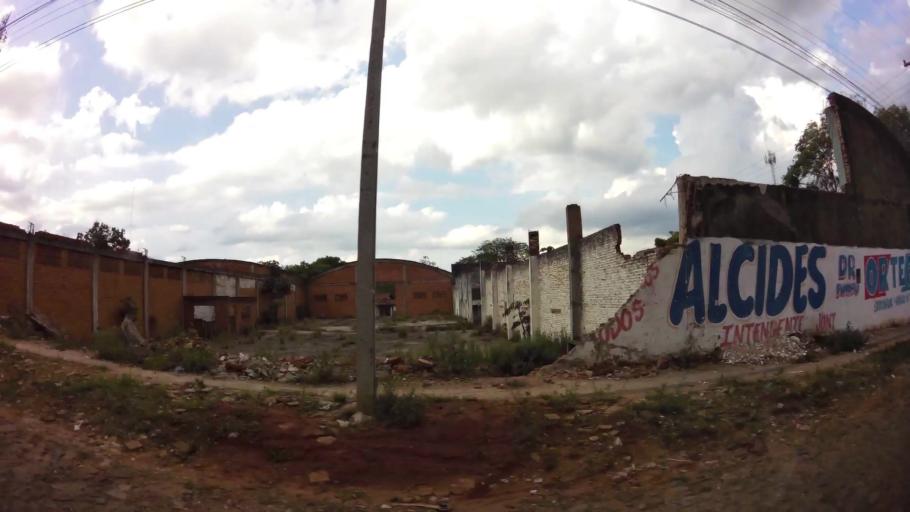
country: PY
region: Central
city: Fernando de la Mora
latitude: -25.3337
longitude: -57.5412
